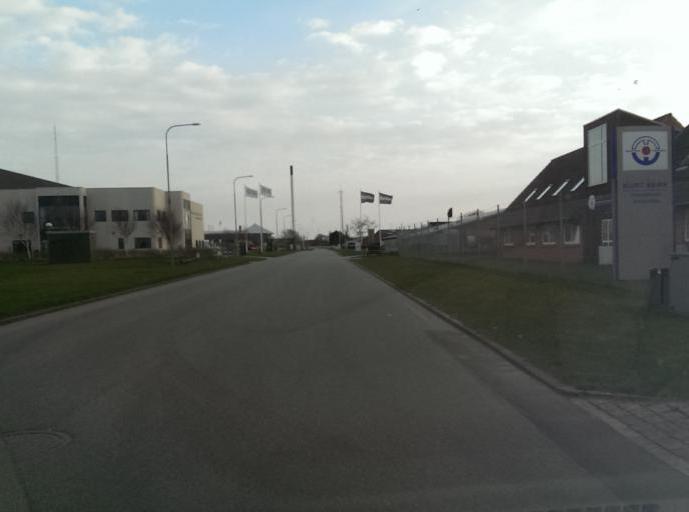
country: DK
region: South Denmark
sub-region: Esbjerg Kommune
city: Esbjerg
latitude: 55.5079
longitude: 8.4097
